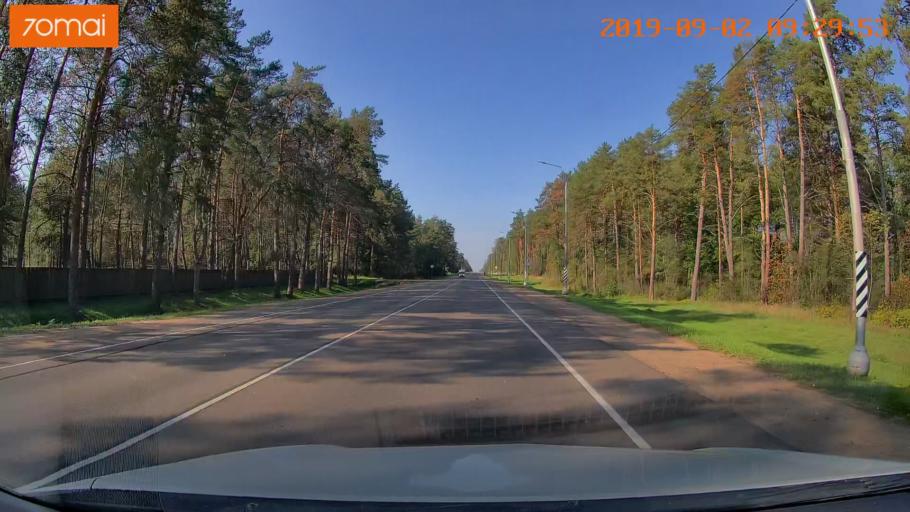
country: RU
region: Kaluga
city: Yukhnov
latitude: 54.7375
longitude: 35.2084
